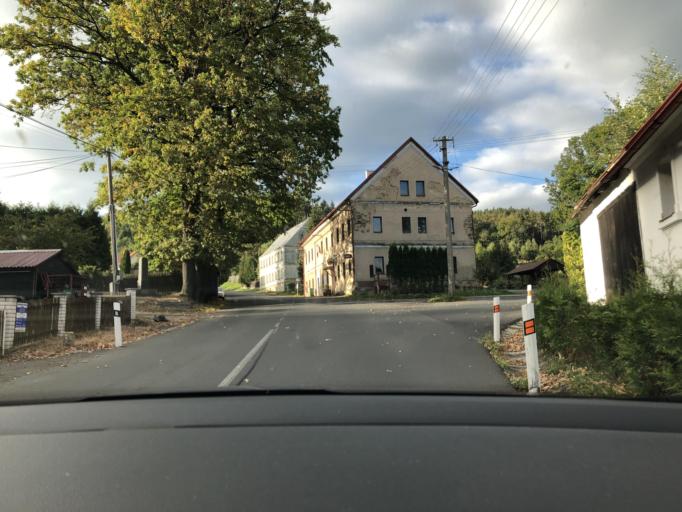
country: CZ
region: Ustecky
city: Zitenice
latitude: 50.6061
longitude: 14.1627
